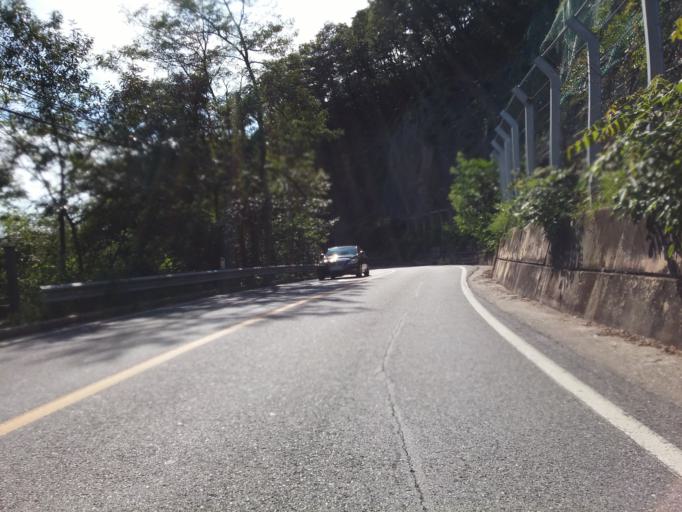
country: KR
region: Daejeon
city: Sintansin
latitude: 36.4790
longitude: 127.4783
